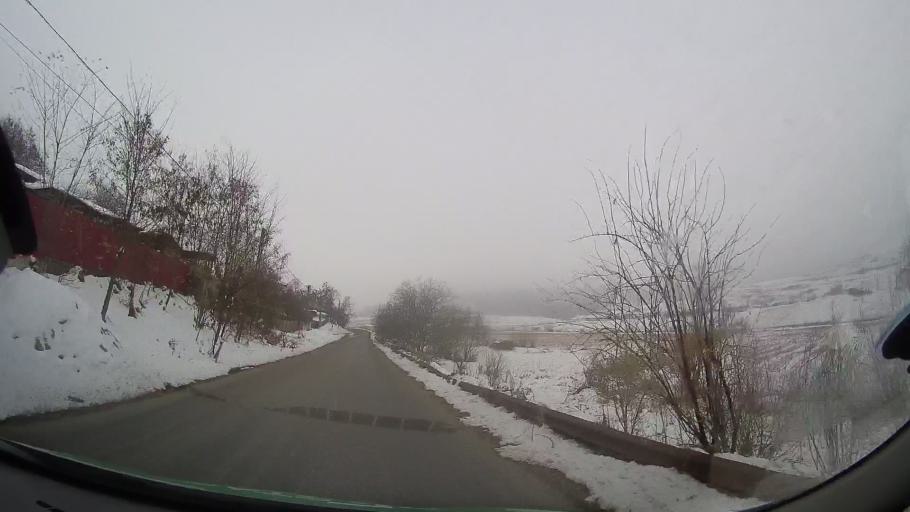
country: RO
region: Bacau
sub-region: Comuna Vultureni
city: Vultureni
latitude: 46.3545
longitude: 27.2894
